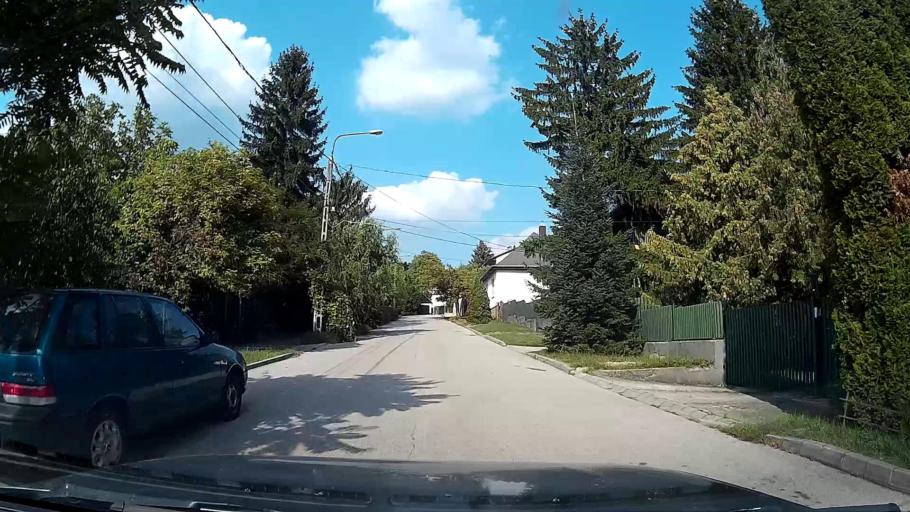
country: HU
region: Pest
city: Budakeszi
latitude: 47.5171
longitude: 18.9303
